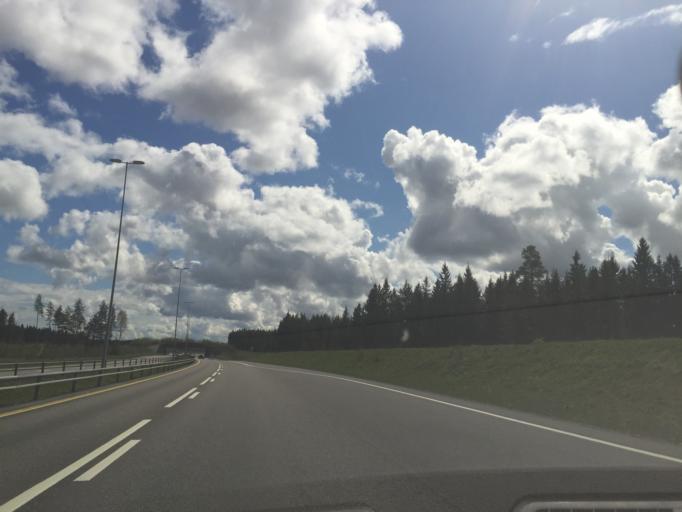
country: NO
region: Akershus
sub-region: Eidsvoll
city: Raholt
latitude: 60.2272
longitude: 11.1743
